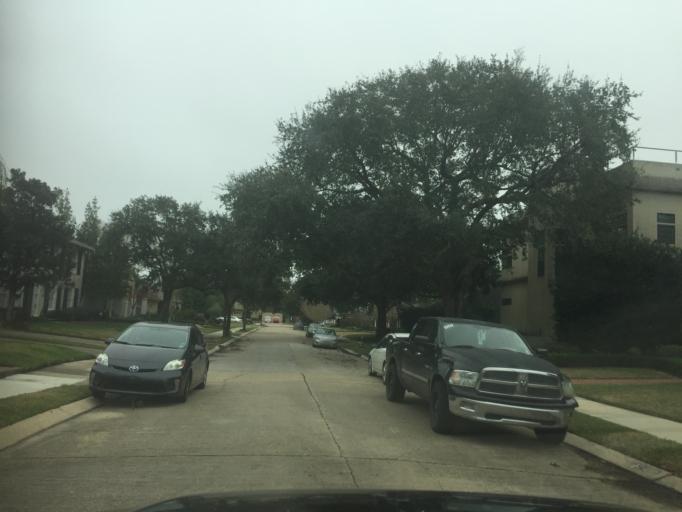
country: US
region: Louisiana
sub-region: Jefferson Parish
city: Metairie
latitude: 30.0200
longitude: -90.1015
